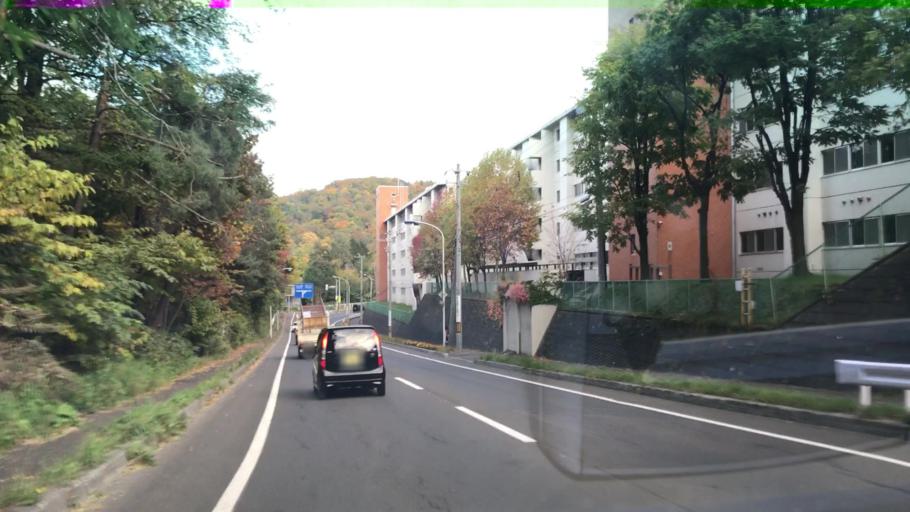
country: JP
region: Hokkaido
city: Sapporo
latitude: 43.0497
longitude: 141.3012
